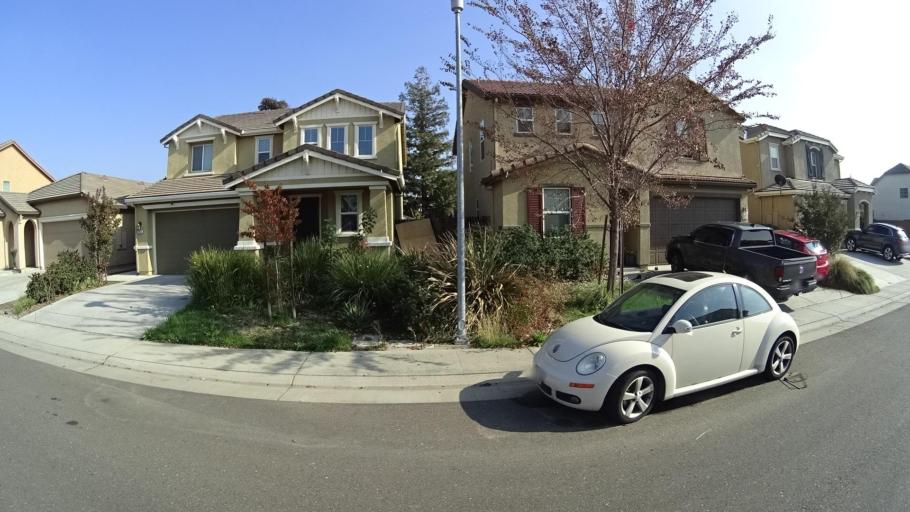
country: US
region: California
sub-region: Sacramento County
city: Vineyard
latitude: 38.4512
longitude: -121.3630
